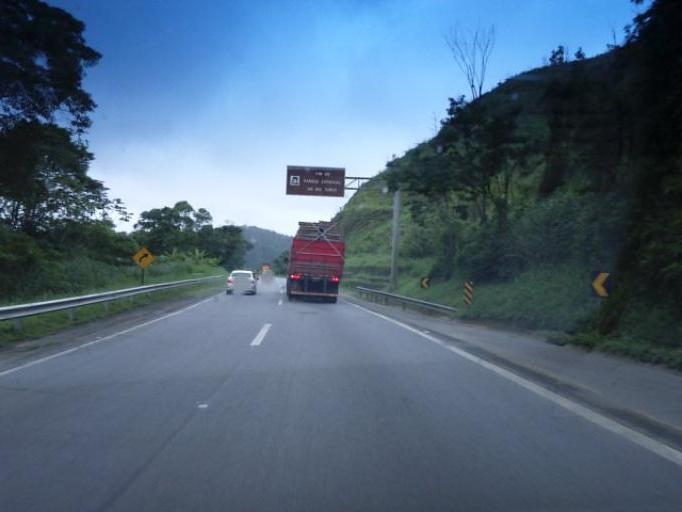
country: BR
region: Sao Paulo
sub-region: Cajati
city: Cajati
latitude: -24.8845
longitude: -48.2241
